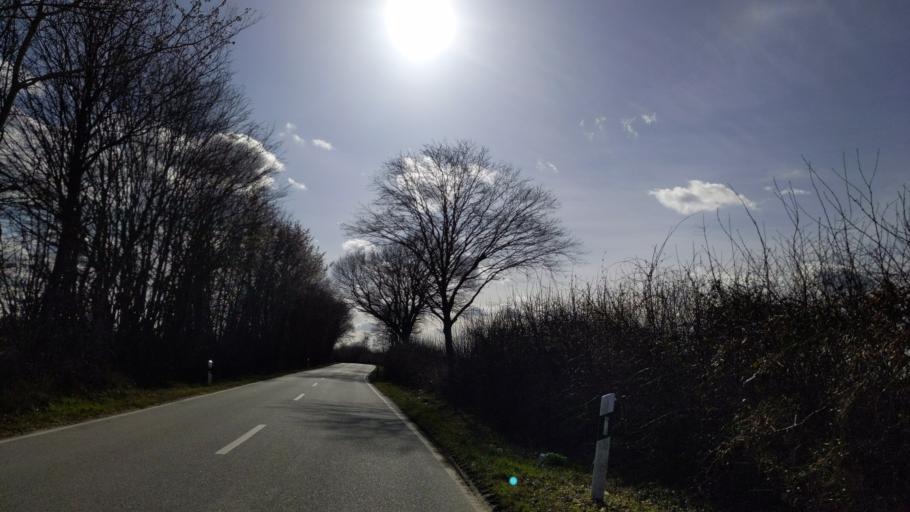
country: DE
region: Schleswig-Holstein
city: Travemuende
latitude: 53.9746
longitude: 10.8457
